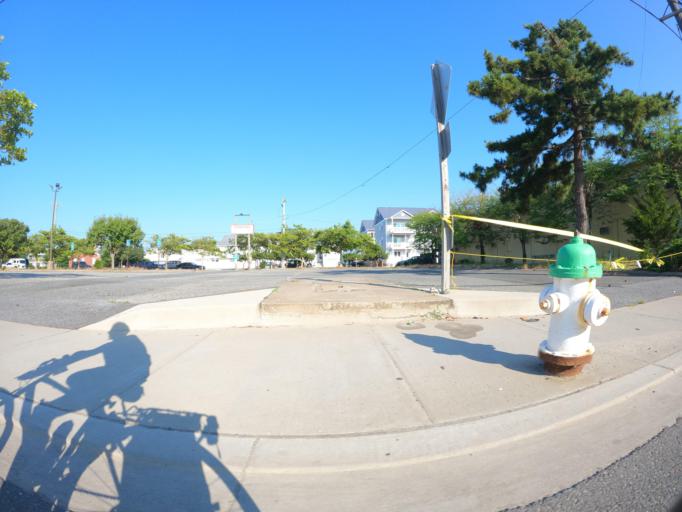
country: US
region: Maryland
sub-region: Worcester County
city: Ocean City
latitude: 38.3499
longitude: -75.0784
